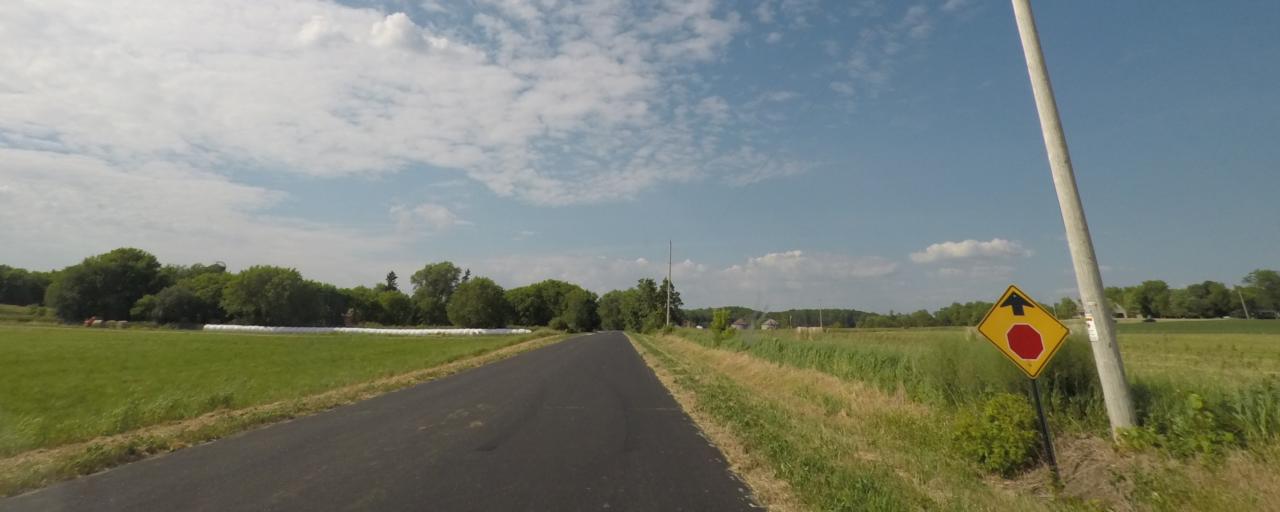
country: US
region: Wisconsin
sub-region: Waukesha County
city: Eagle
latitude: 42.7911
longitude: -88.5289
